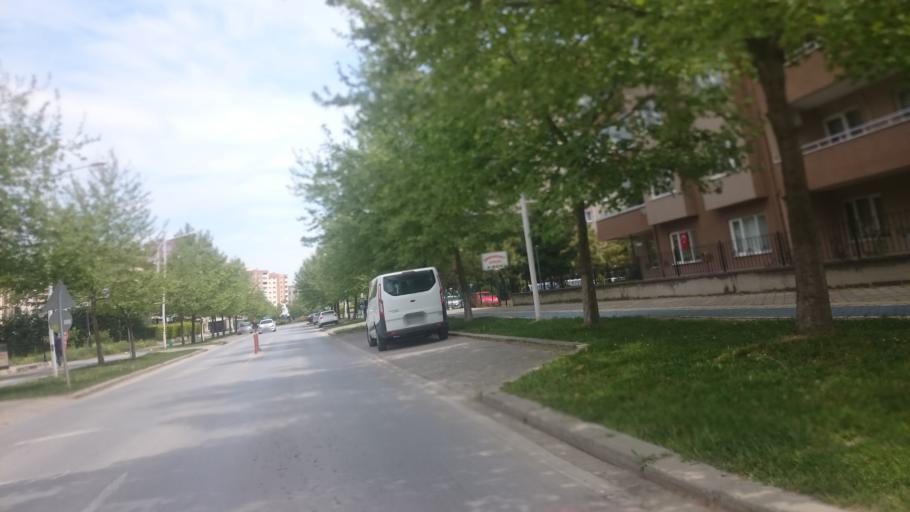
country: TR
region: Bursa
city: Cali
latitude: 40.2258
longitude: 28.9073
